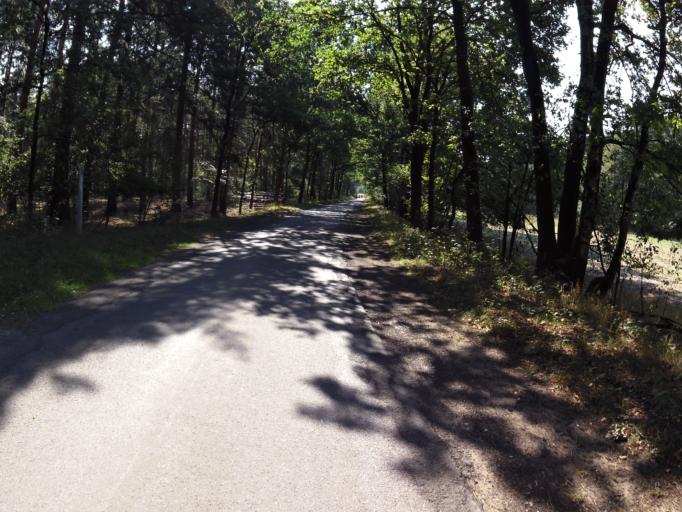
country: DE
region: North Rhine-Westphalia
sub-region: Regierungsbezirk Detmold
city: Harsewinkel
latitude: 51.9493
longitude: 8.2359
